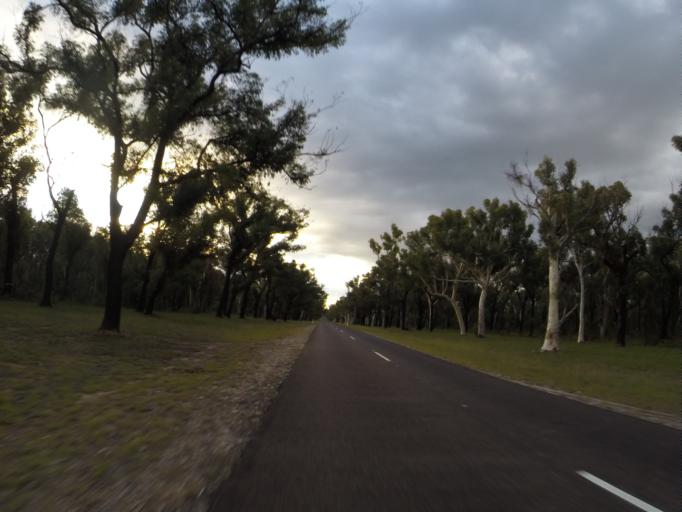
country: AU
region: New South Wales
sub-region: Wollondilly
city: Buxton
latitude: -34.3216
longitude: 150.6202
